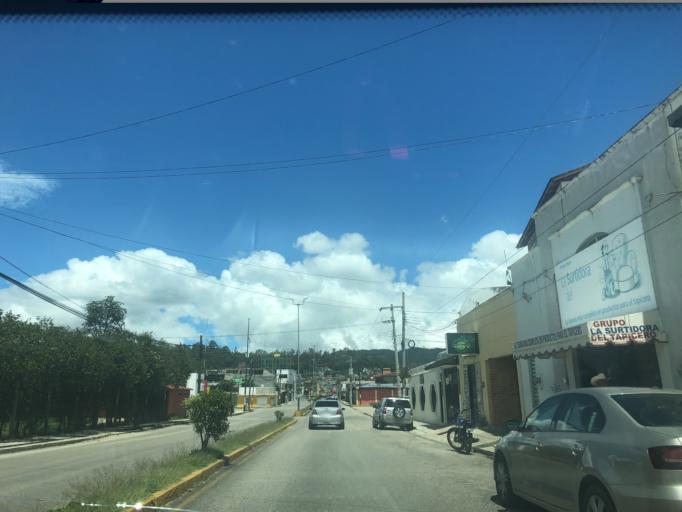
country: MX
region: Chiapas
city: San Cristobal de las Casas
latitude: 16.7233
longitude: -92.6402
